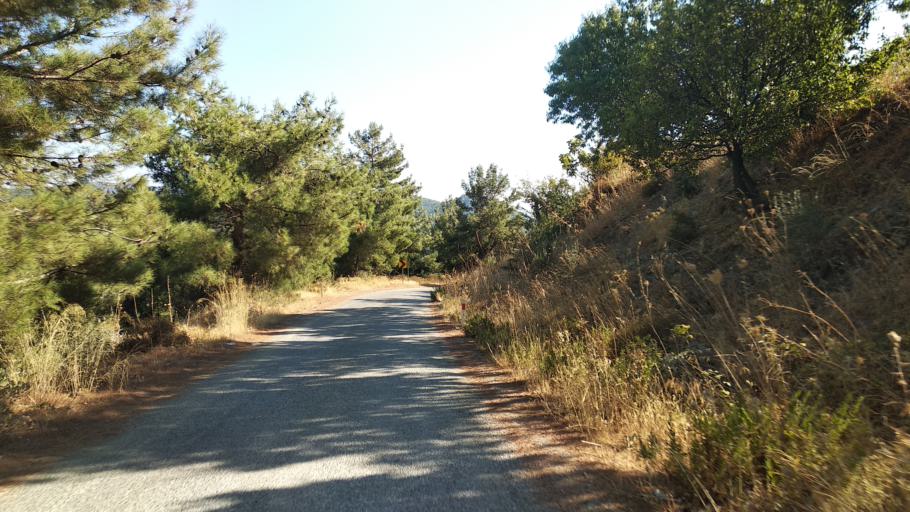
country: TR
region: Izmir
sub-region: Seferihisar
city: Seferhisar
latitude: 38.3269
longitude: 26.9423
